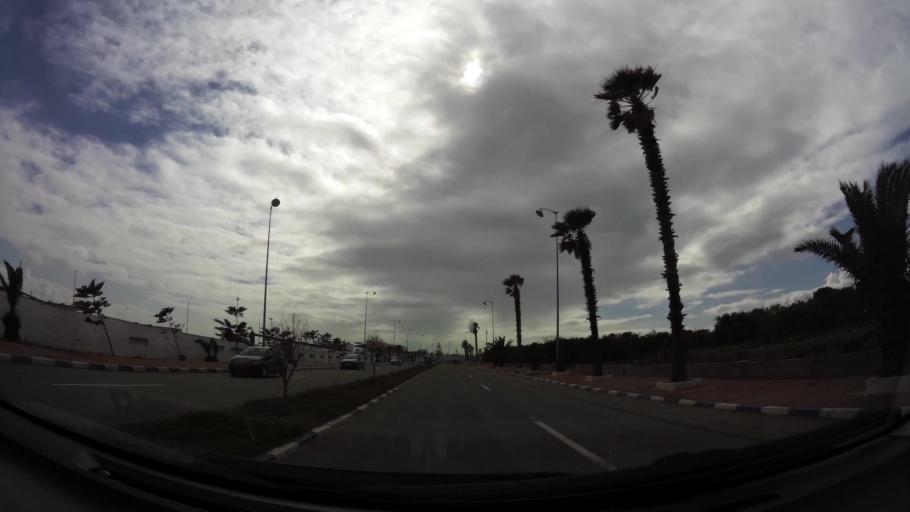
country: MA
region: Doukkala-Abda
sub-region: El-Jadida
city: El Jadida
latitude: 33.2448
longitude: -8.4627
